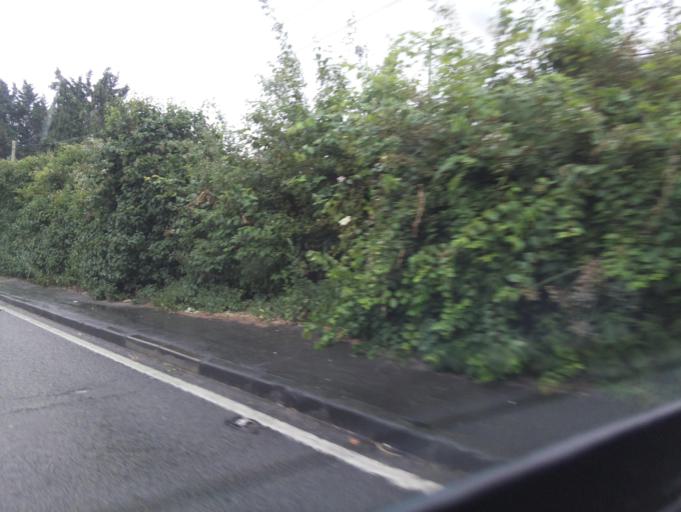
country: GB
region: England
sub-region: Surrey
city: Salfords
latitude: 51.2205
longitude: -0.1719
